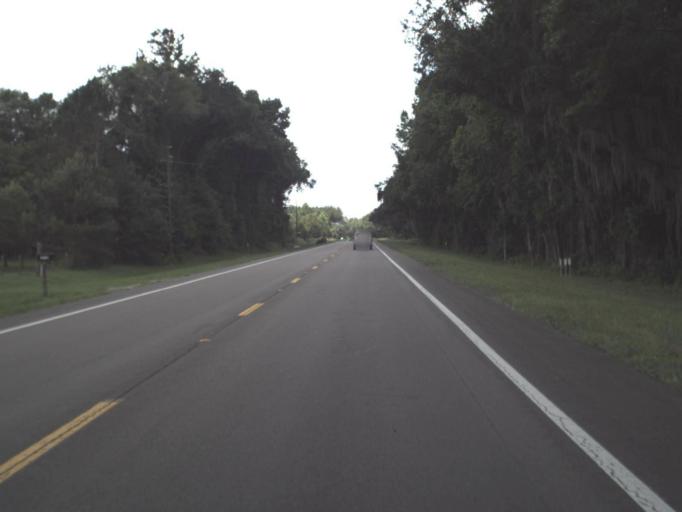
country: US
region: Florida
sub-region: Alachua County
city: Alachua
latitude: 29.7949
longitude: -82.3826
